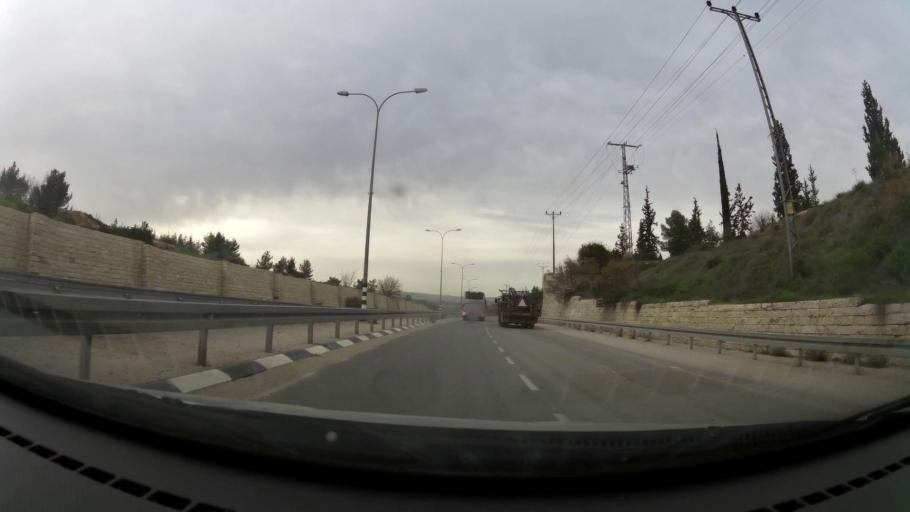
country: IL
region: Jerusalem
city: Bet Shemesh
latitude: 31.6980
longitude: 35.0096
